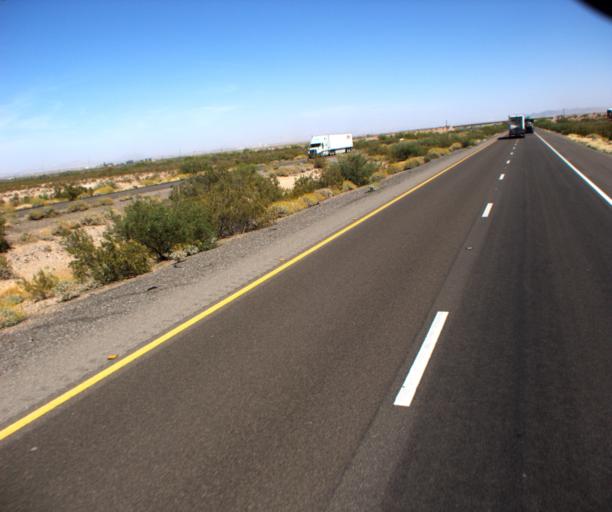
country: US
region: Arizona
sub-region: Pinal County
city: Casa Grande
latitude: 32.8281
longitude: -111.9699
